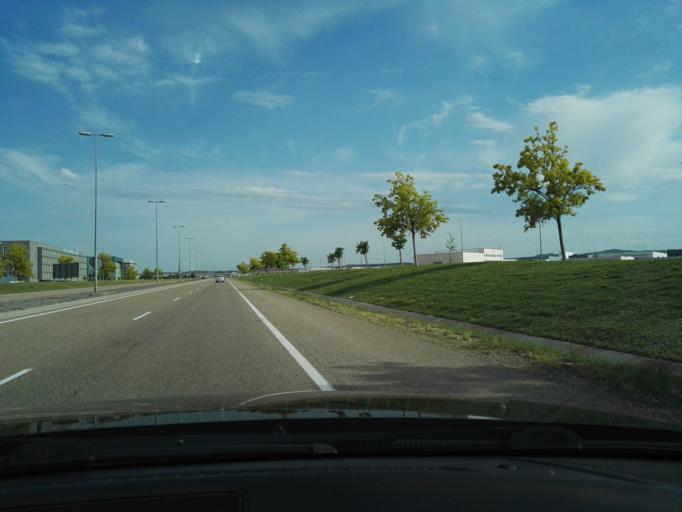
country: ES
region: Aragon
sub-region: Provincia de Zaragoza
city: Montecanal
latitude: 41.6448
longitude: -0.9953
